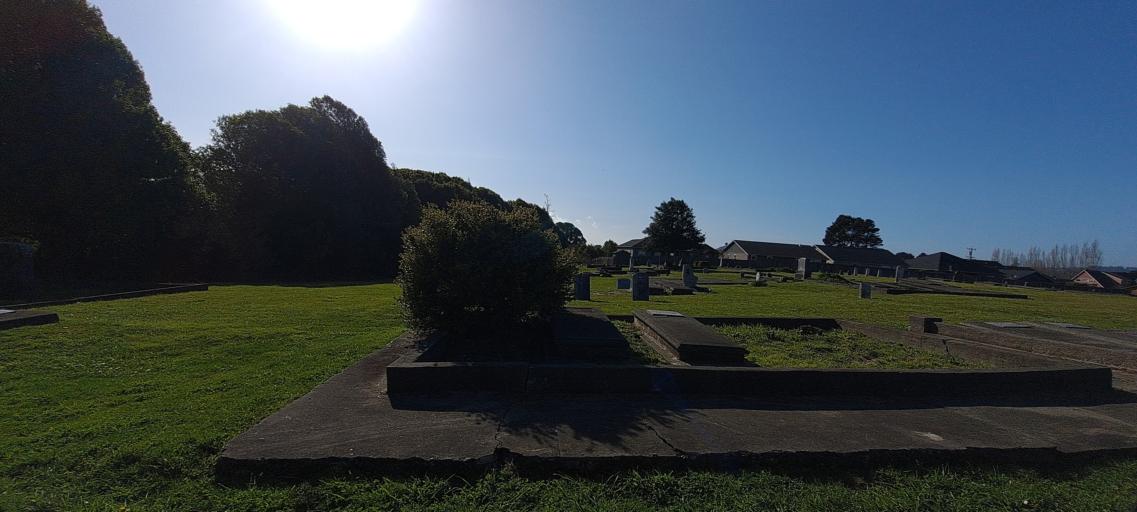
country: US
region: California
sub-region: Humboldt County
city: Fortuna
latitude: 40.5729
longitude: -124.1330
